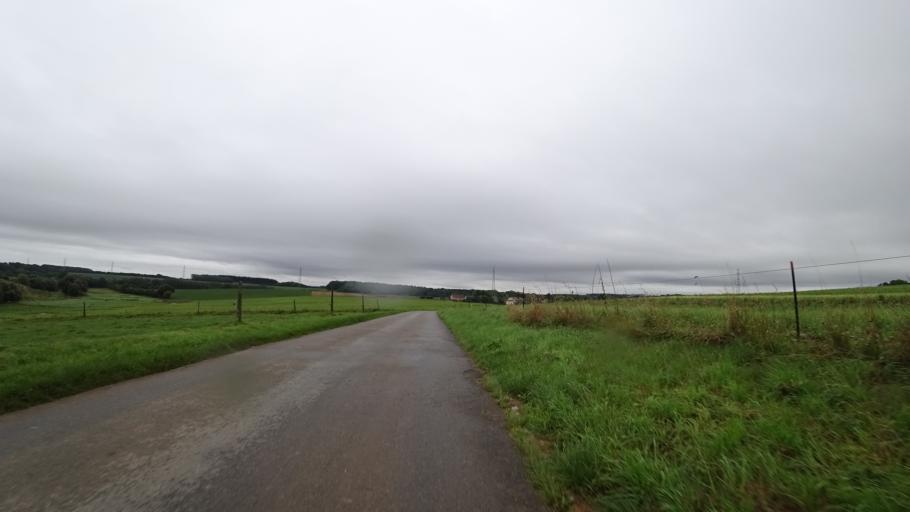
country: BE
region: Wallonia
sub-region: Province de Namur
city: Namur
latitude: 50.5165
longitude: 4.8058
